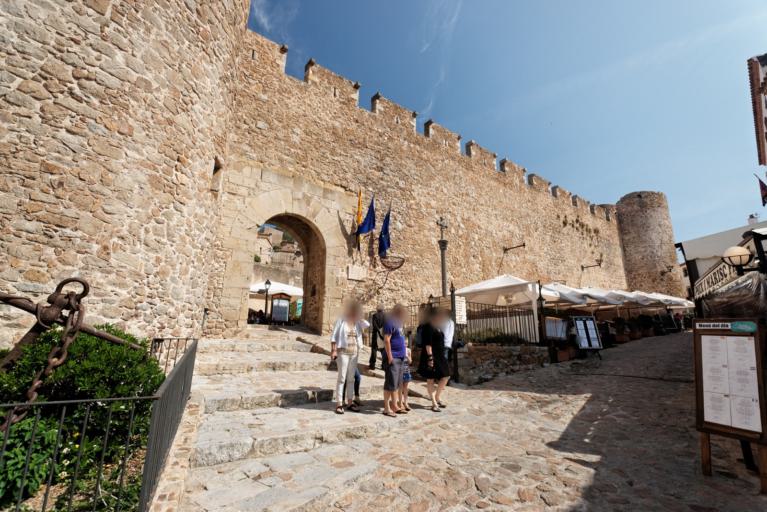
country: ES
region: Catalonia
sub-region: Provincia de Girona
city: Tossa de Mar
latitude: 41.7169
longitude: 2.9325
